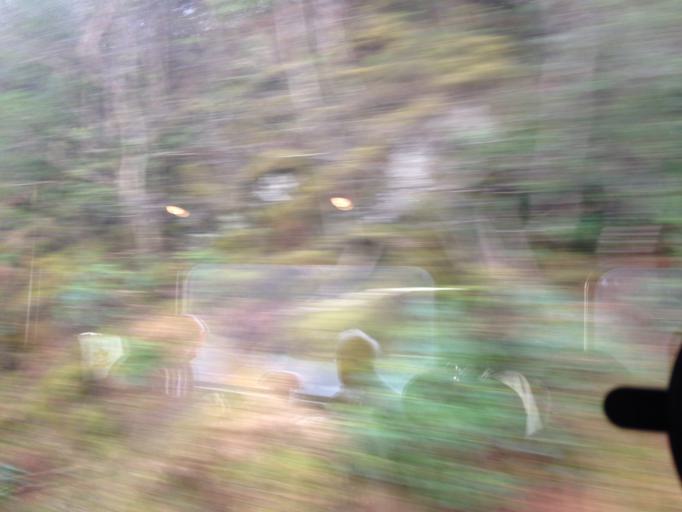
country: GB
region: Scotland
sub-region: Argyll and Bute
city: Garelochhead
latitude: 56.1733
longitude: -4.7769
